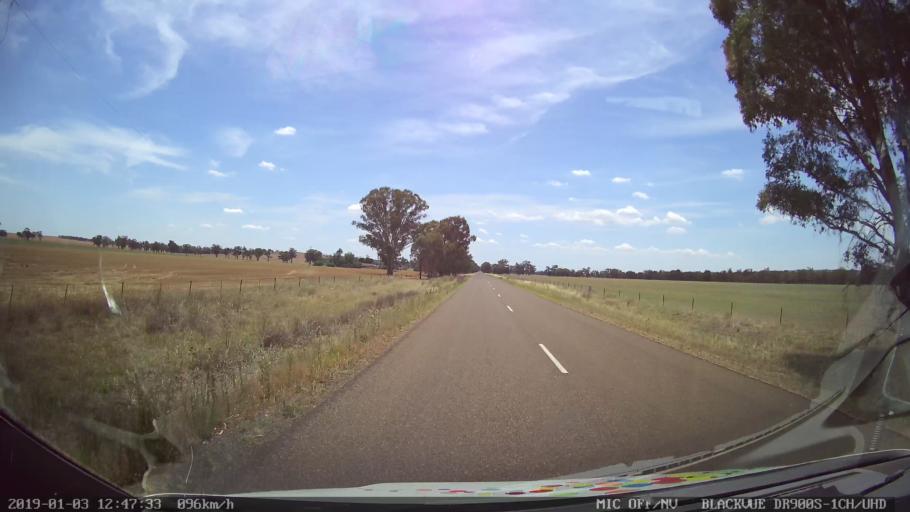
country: AU
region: New South Wales
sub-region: Weddin
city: Grenfell
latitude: -33.7253
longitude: 148.2429
